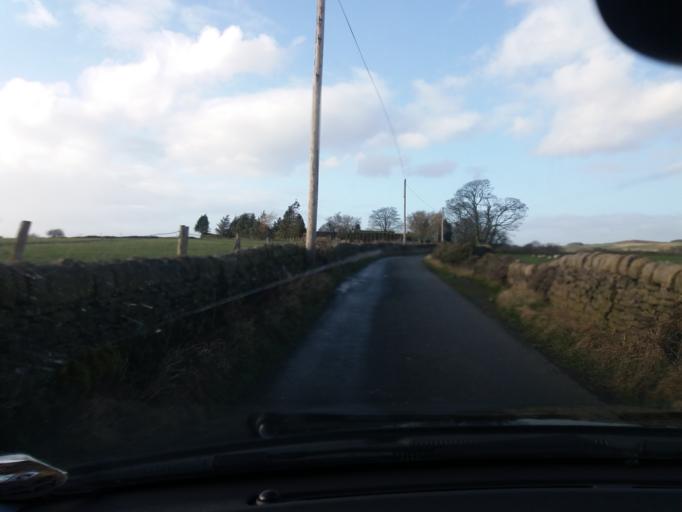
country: GB
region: England
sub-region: Lancashire
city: Adlington
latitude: 53.6349
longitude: -2.5817
